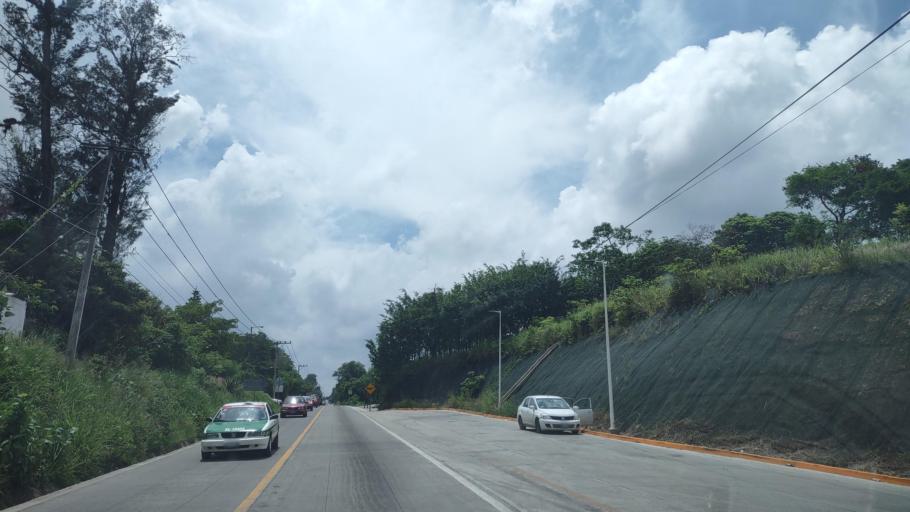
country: MX
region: Veracruz
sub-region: Emiliano Zapata
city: Jacarandas
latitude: 19.4700
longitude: -96.8503
